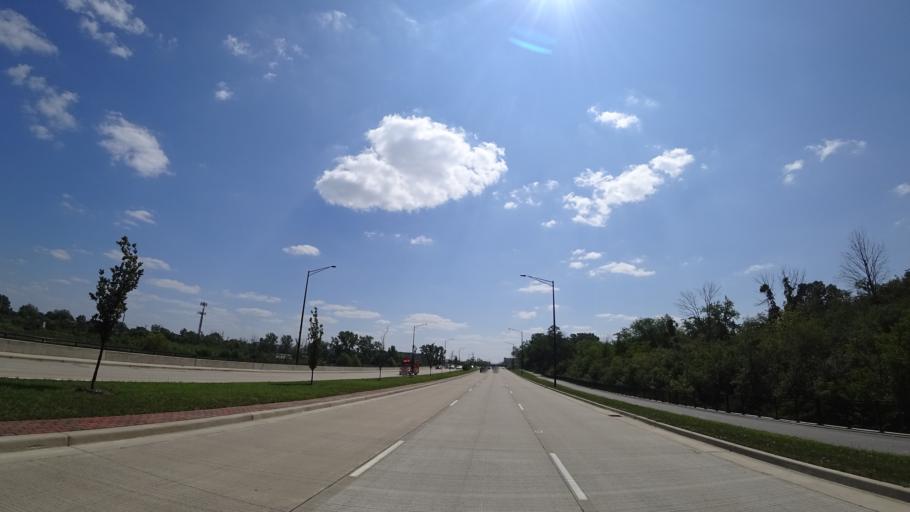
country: US
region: Illinois
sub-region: Cook County
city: Orland Park
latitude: 41.6403
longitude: -87.8540
